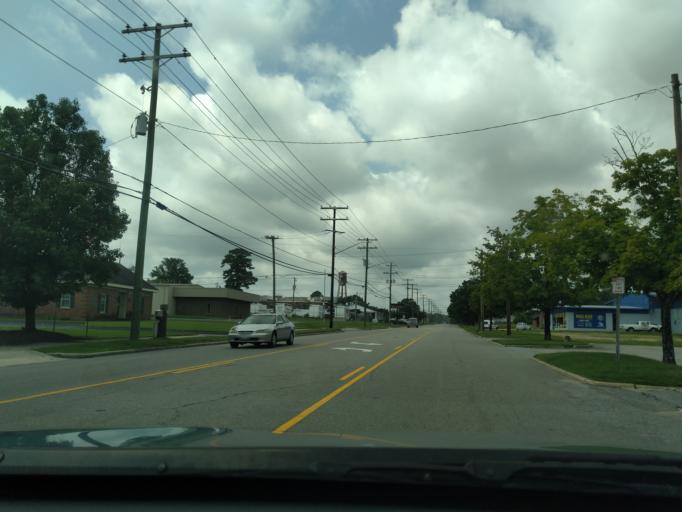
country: US
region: North Carolina
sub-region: Edgecombe County
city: Tarboro
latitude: 35.8979
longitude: -77.5406
